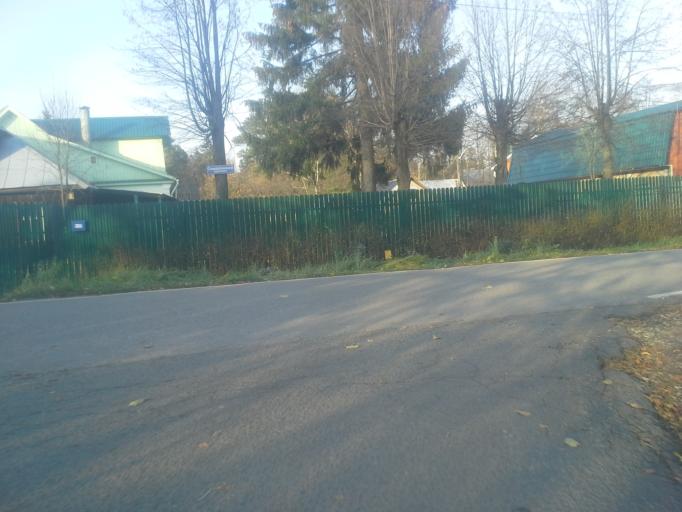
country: RU
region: Moskovskaya
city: Golitsyno
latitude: 55.6093
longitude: 36.9940
